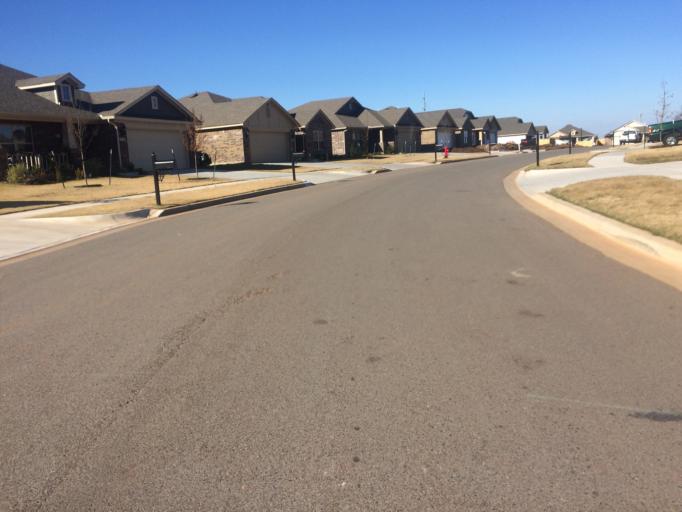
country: US
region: Oklahoma
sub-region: Cleveland County
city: Norman
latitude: 35.2526
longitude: -97.4558
